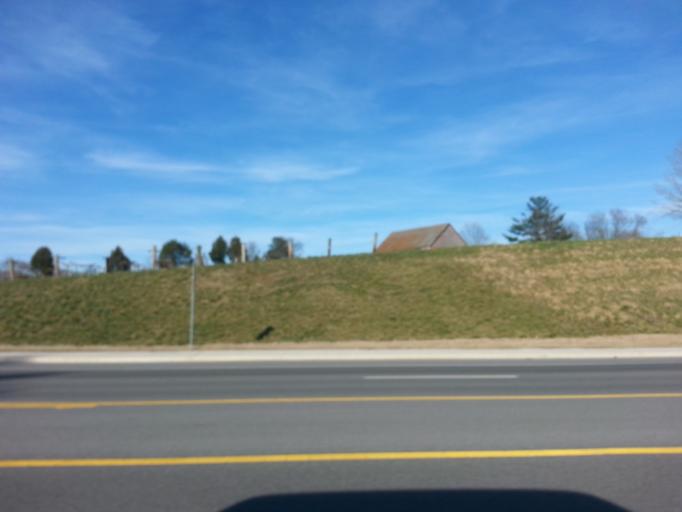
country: US
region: Tennessee
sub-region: Warren County
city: McMinnville
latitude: 35.7005
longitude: -85.8271
